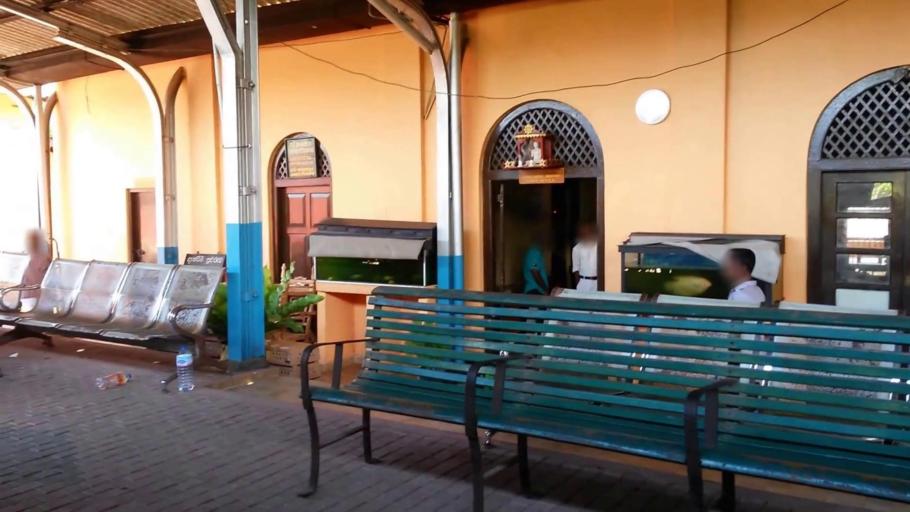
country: LK
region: Southern
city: Hikkaduwa
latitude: 6.1470
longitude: 80.0999
